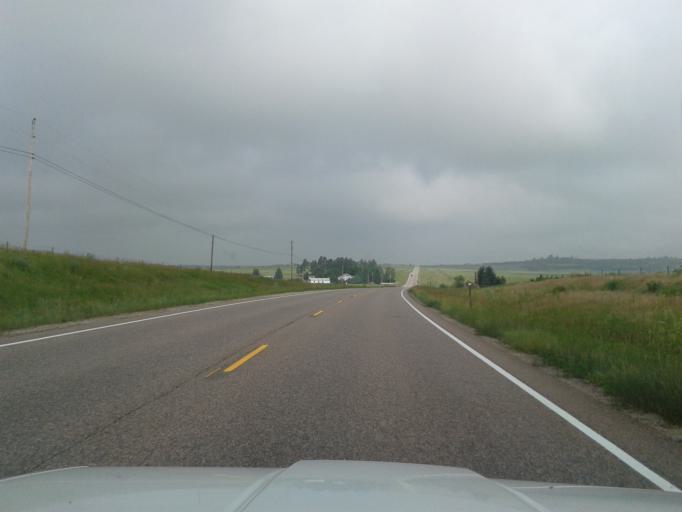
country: US
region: Colorado
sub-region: Elbert County
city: Elizabeth
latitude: 39.2628
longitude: -104.7129
